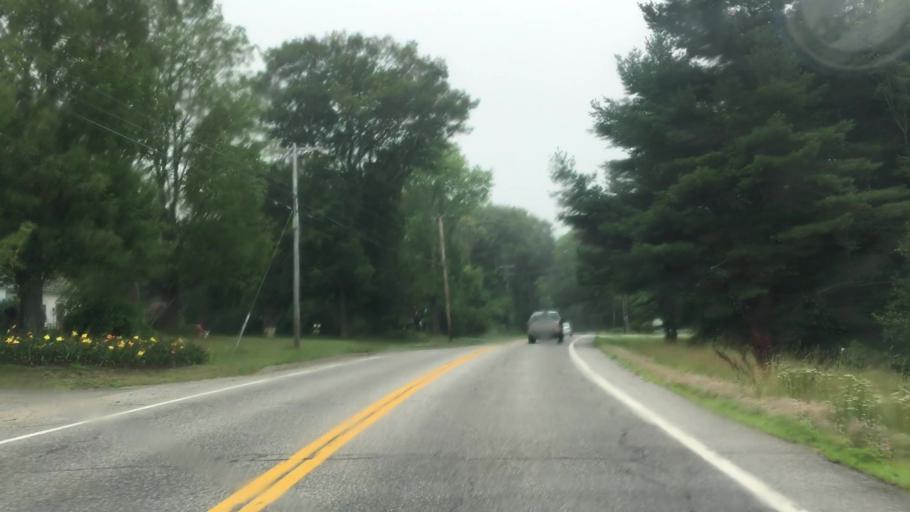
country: US
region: Maine
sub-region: Lincoln County
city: Wiscasset
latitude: 43.9933
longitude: -69.6365
